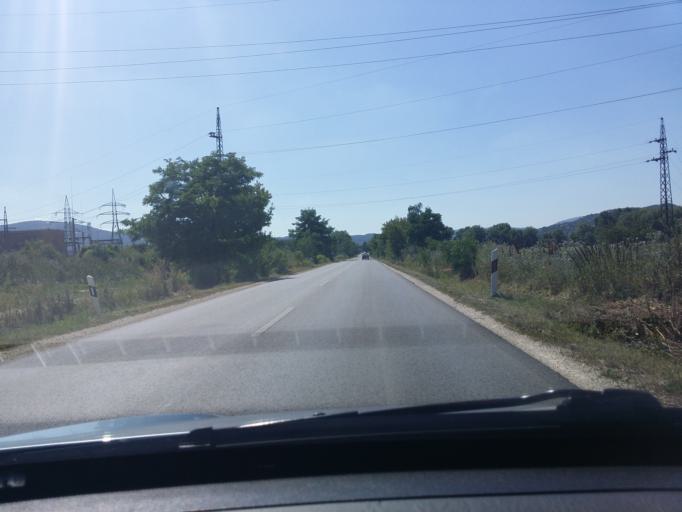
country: HU
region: Pest
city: Pomaz
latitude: 47.6457
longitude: 19.0499
